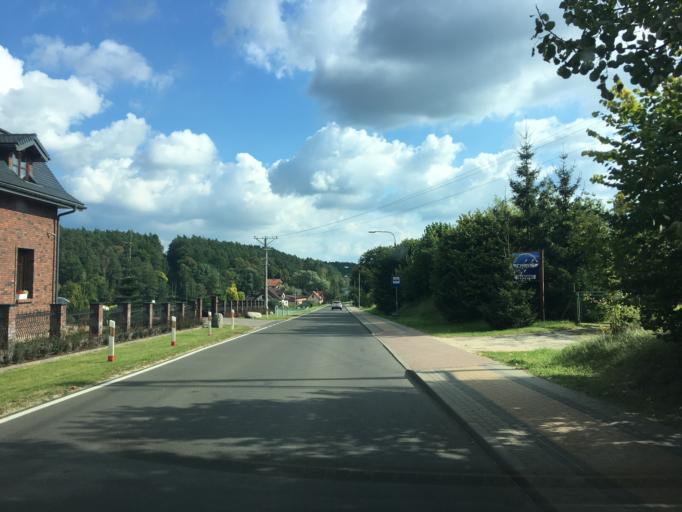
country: PL
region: Kujawsko-Pomorskie
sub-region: Powiat swiecki
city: Osie
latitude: 53.6197
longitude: 18.2666
